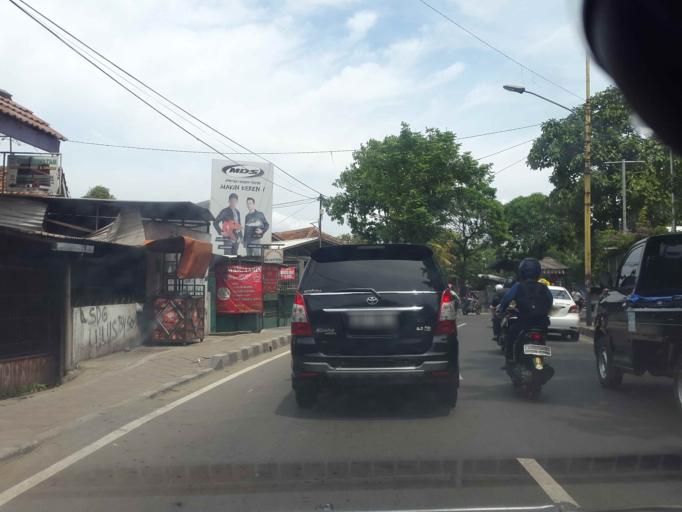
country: ID
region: Banten
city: Tangerang
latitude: -6.1685
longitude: 106.6265
